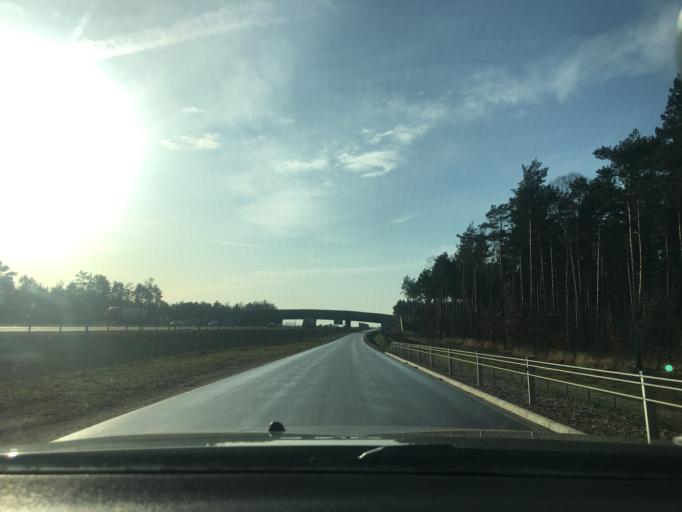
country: PL
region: Swietokrzyskie
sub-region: Powiat jedrzejowski
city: Jedrzejow
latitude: 50.6751
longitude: 20.3474
